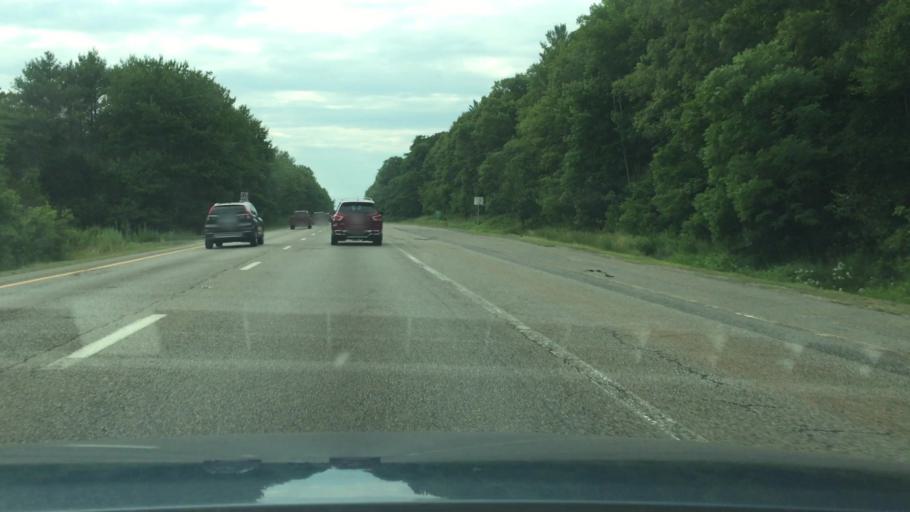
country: US
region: Massachusetts
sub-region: Plymouth County
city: Hanover
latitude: 42.1303
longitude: -70.8062
